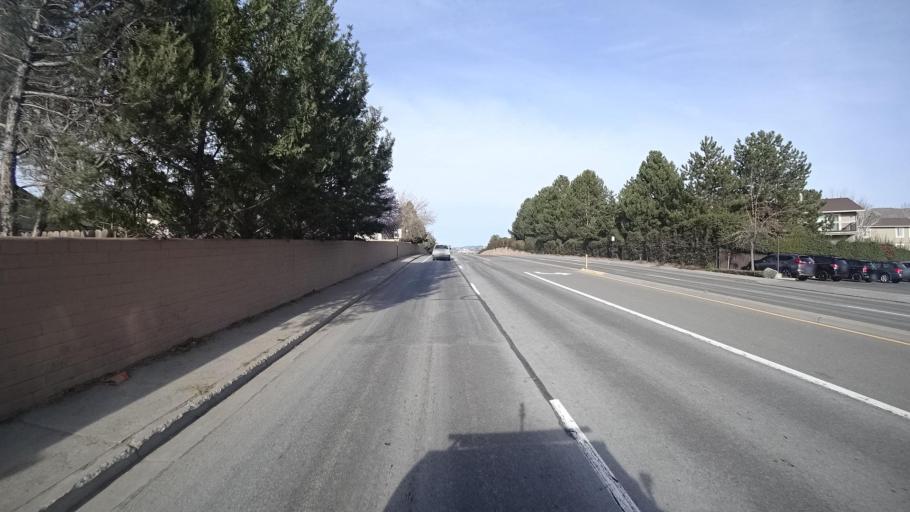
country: US
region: Nevada
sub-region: Washoe County
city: Reno
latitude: 39.5334
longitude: -119.8697
